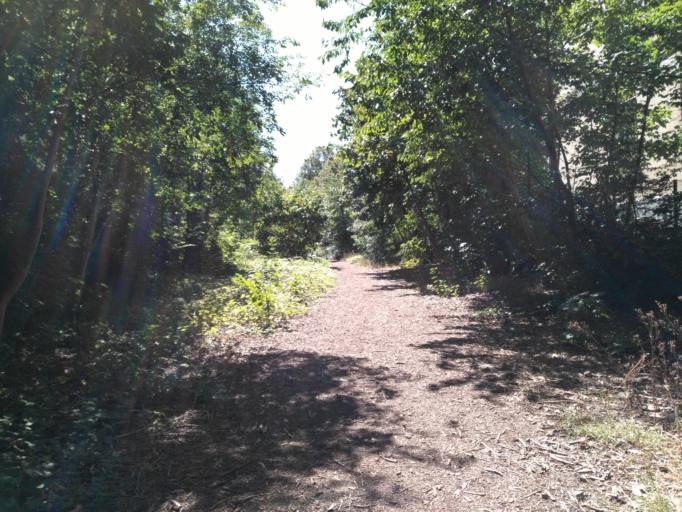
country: FR
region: Ile-de-France
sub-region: Departement des Hauts-de-Seine
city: Boulogne-Billancourt
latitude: 48.8555
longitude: 2.2641
